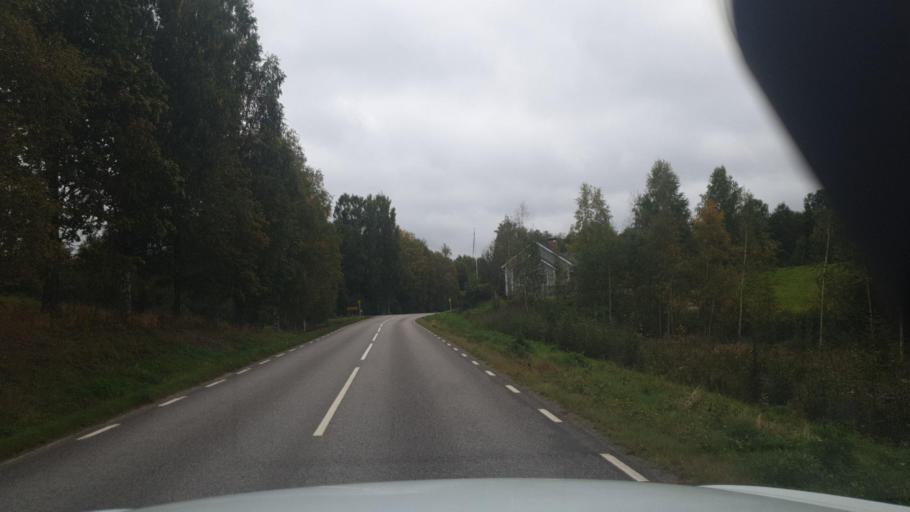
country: SE
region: Vaermland
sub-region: Sunne Kommun
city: Sunne
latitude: 59.8014
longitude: 13.0501
